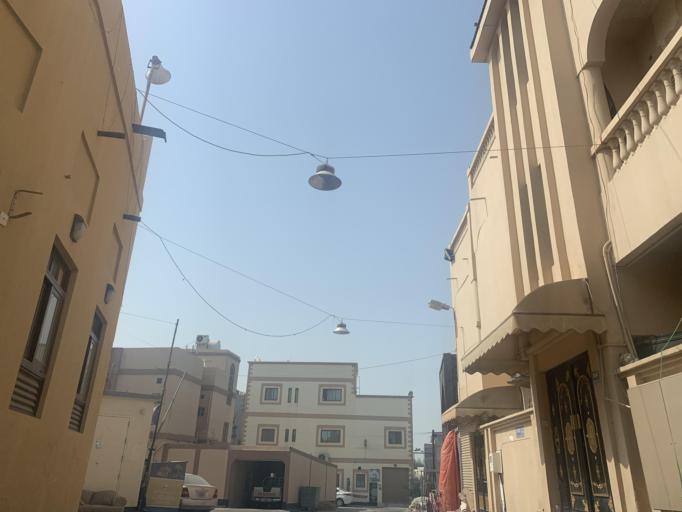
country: BH
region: Manama
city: Jidd Hafs
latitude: 26.2120
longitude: 50.4623
